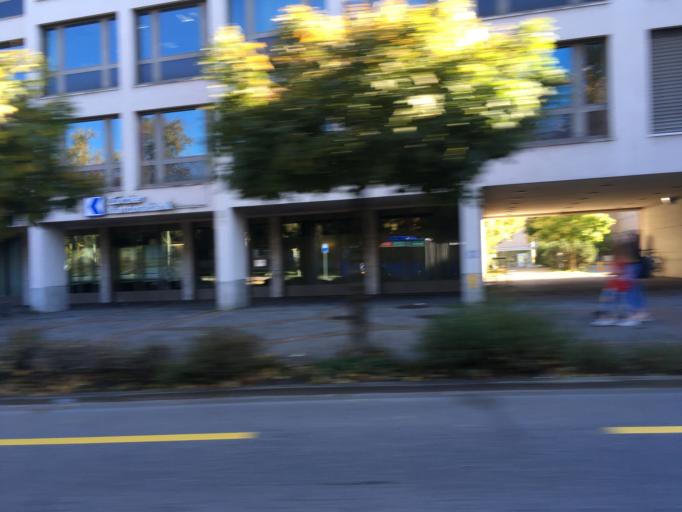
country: CH
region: Zurich
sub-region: Bezirk Hinwil
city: Wetzikon / Ober-Wetzikon
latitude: 47.3269
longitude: 8.8011
